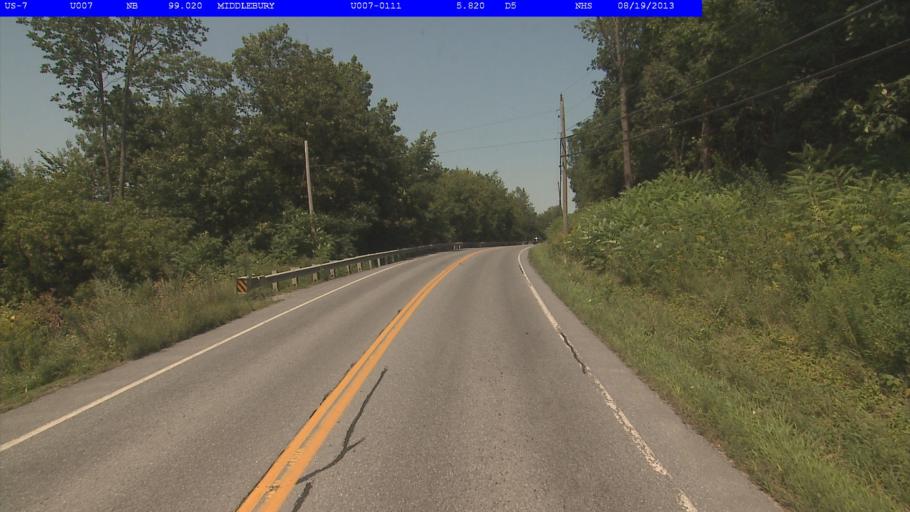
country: US
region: Vermont
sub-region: Addison County
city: Middlebury (village)
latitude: 44.0244
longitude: -73.1667
